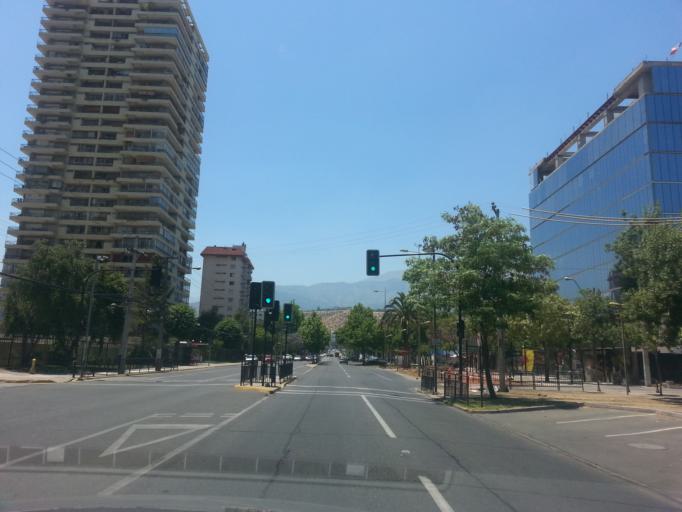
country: CL
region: Santiago Metropolitan
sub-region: Provincia de Santiago
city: Villa Presidente Frei, Nunoa, Santiago, Chile
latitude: -33.4083
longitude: -70.5497
